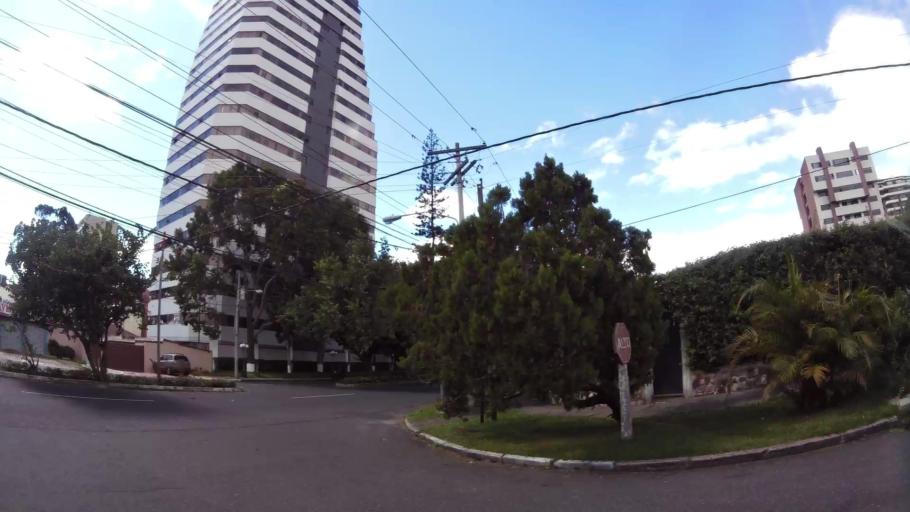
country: GT
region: Guatemala
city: Santa Catarina Pinula
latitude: 14.5792
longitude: -90.5183
